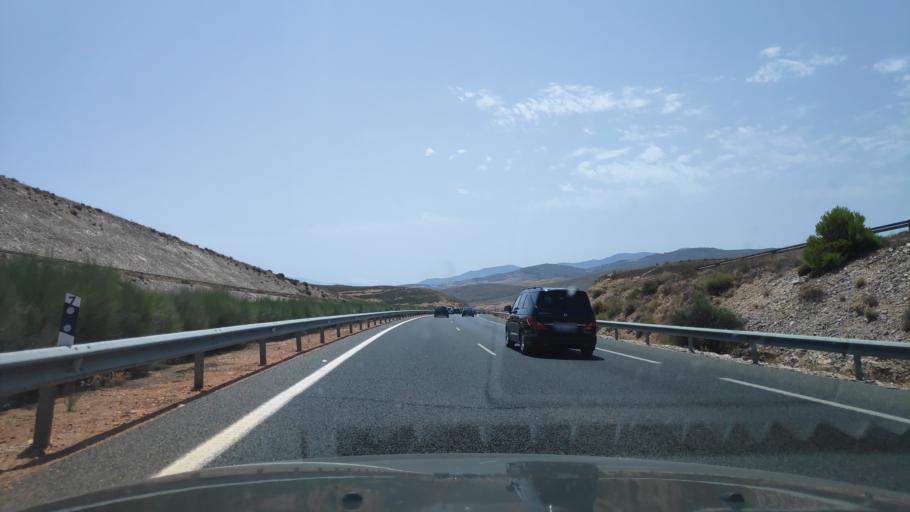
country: ES
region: Andalusia
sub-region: Provincia de Granada
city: Padul
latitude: 37.0005
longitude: -3.6313
